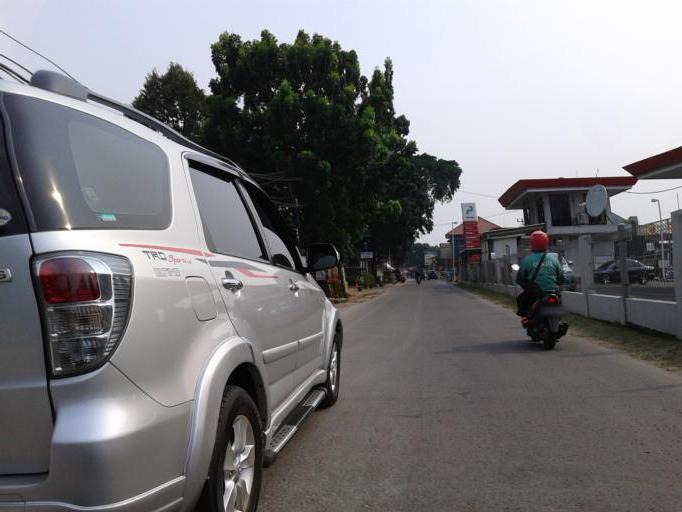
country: ID
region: West Java
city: Pamulang
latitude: -6.3423
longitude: 106.7792
